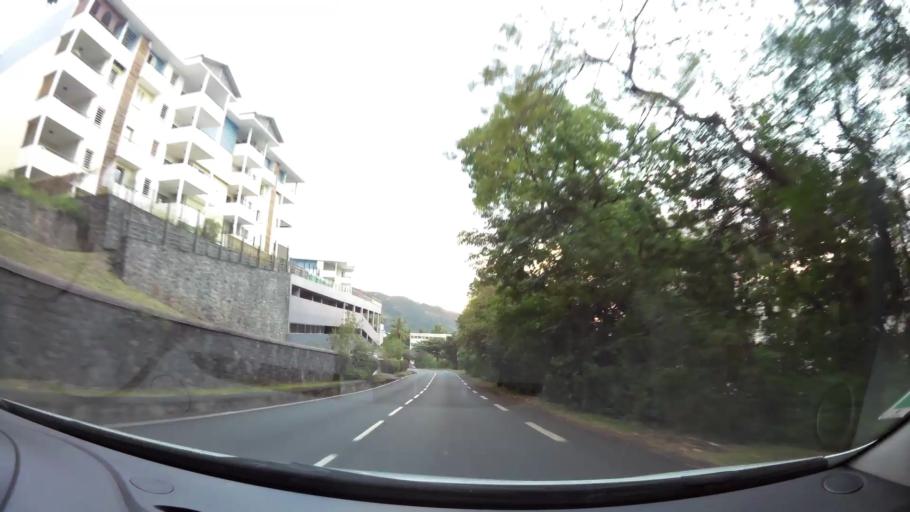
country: RE
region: Reunion
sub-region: Reunion
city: Saint-Denis
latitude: -20.8999
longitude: 55.4634
